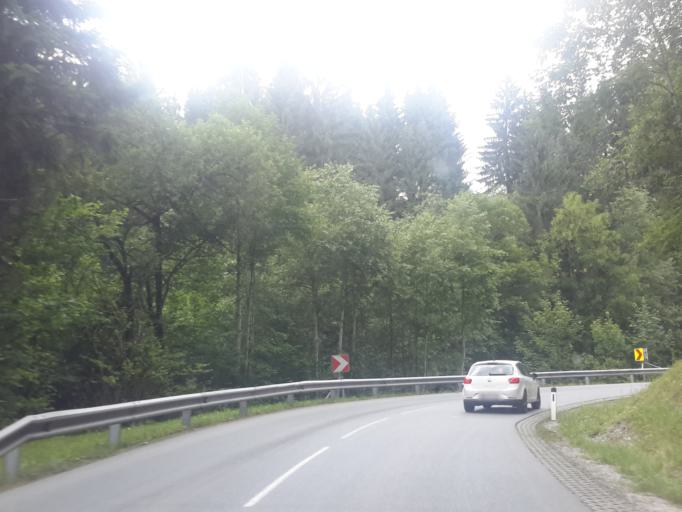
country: AT
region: Tyrol
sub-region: Politischer Bezirk Kitzbuhel
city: Oberndorf in Tirol
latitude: 47.5008
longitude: 12.3548
